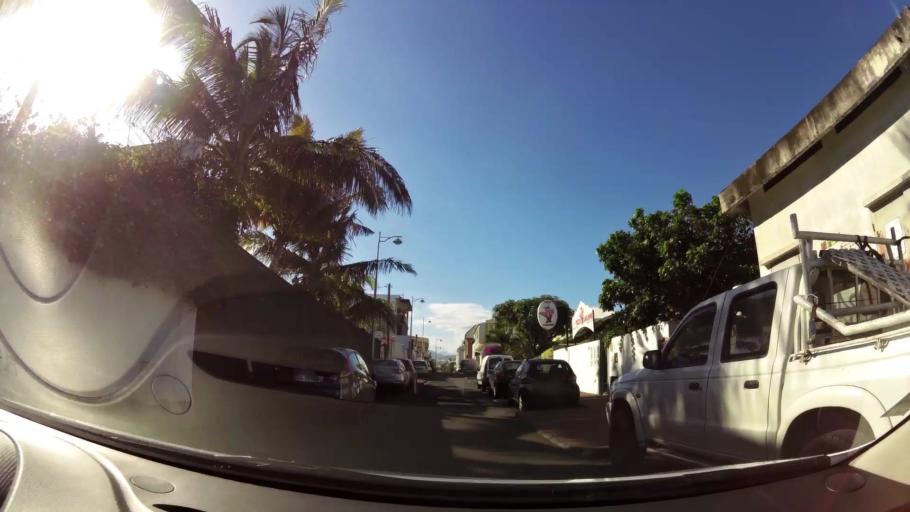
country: RE
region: Reunion
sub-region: Reunion
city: Saint-Pierre
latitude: -21.3417
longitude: 55.4699
